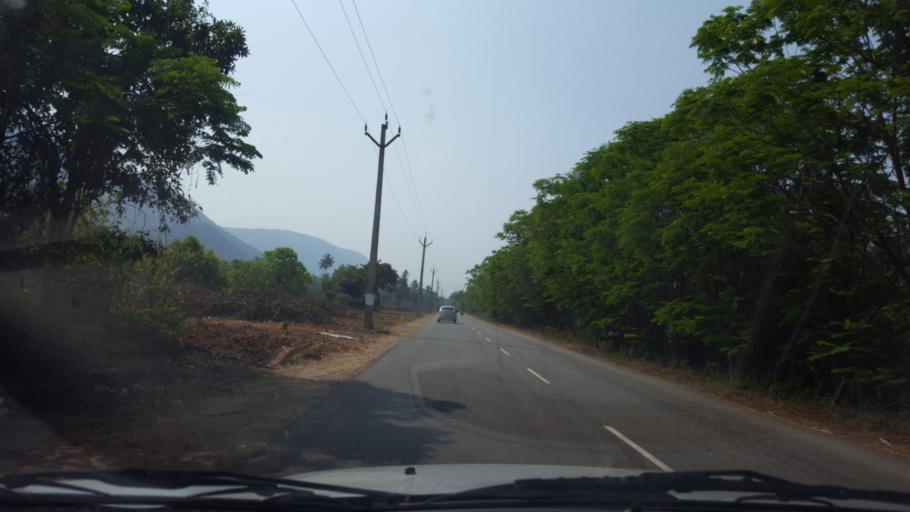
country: IN
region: Andhra Pradesh
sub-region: Vishakhapatnam
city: Vepagunta
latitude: 17.8440
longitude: 83.2664
